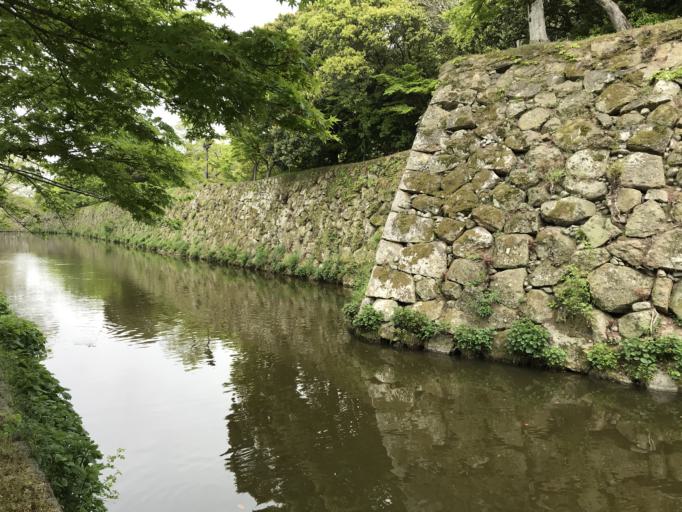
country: JP
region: Hyogo
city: Himeji
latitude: 34.8395
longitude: 134.6902
